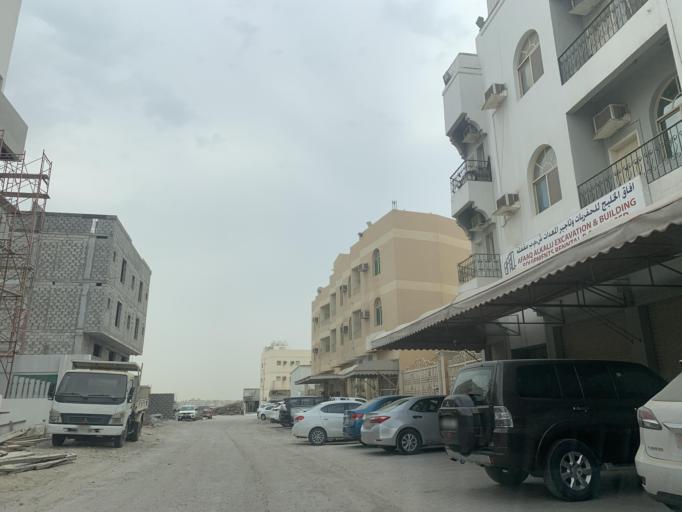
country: BH
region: Northern
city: Madinat `Isa
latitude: 26.1791
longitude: 50.5116
